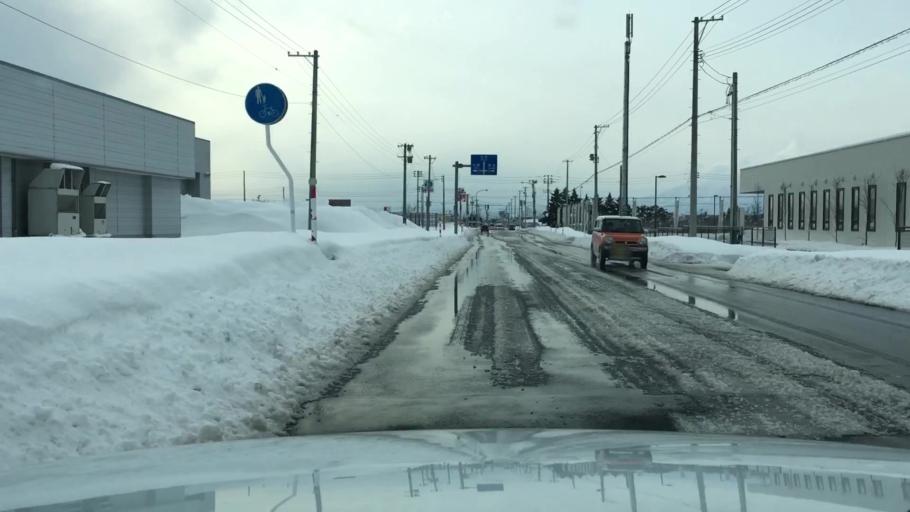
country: JP
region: Aomori
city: Kuroishi
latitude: 40.5917
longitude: 140.5714
